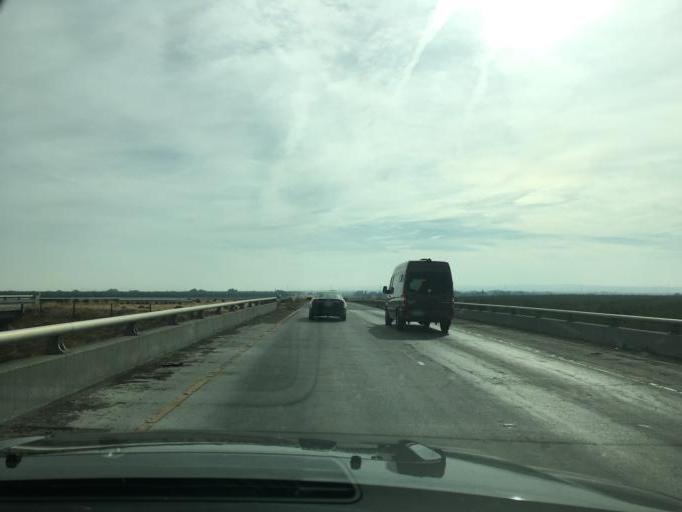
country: US
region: California
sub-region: Fresno County
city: Huron
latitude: 36.1769
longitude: -120.1948
